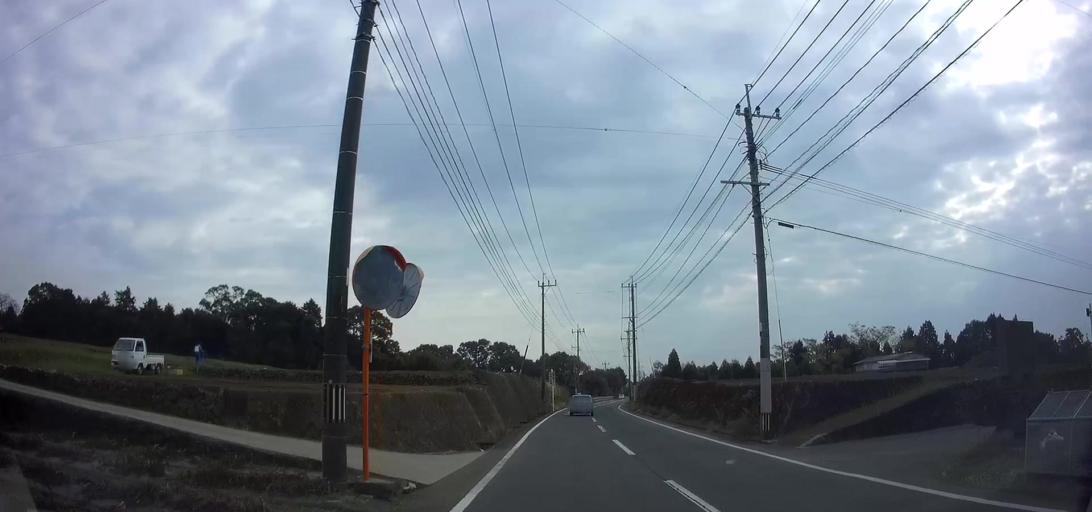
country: JP
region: Nagasaki
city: Shimabara
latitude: 32.6925
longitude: 130.3011
